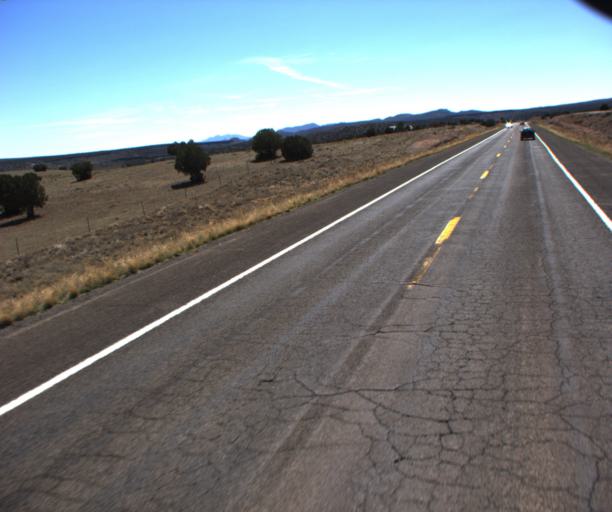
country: US
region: Arizona
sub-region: Mohave County
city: Peach Springs
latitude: 35.4634
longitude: -113.6076
